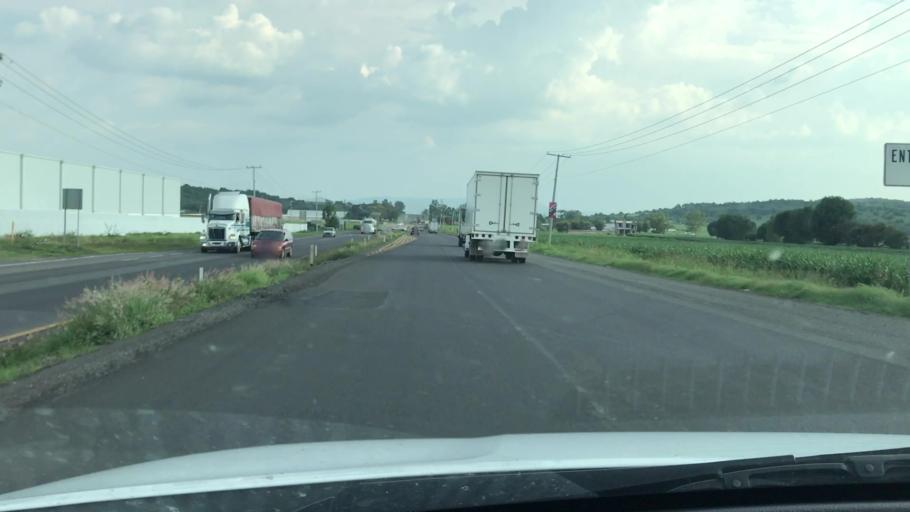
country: MX
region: Guanajuato
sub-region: Irapuato
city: San Ignacio de Rivera (Ojo de Agua)
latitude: 20.5548
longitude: -101.4514
